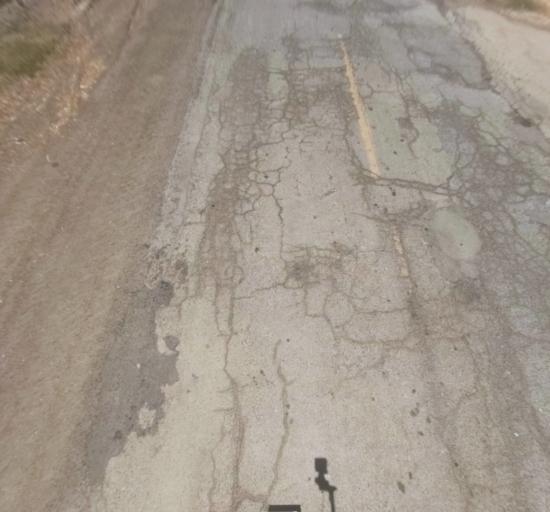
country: US
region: California
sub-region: Madera County
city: Chowchilla
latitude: 37.0093
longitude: -120.3466
